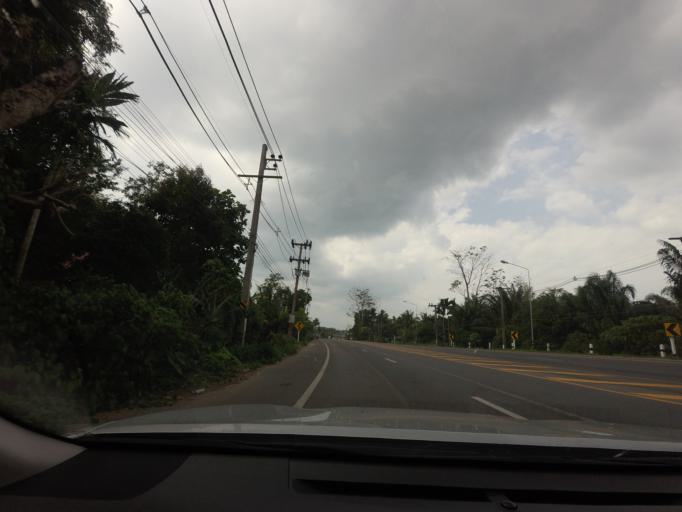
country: TH
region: Phangnga
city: Ban Ao Nang
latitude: 8.0522
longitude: 98.7706
